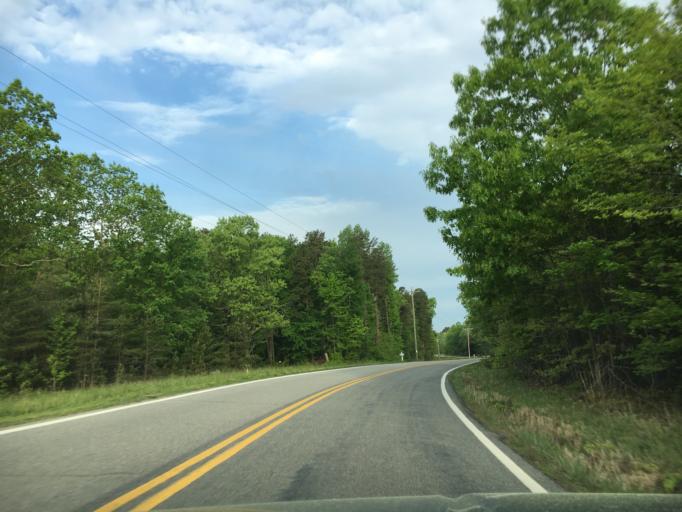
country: US
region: Virginia
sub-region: Halifax County
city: Halifax
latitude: 36.8898
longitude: -78.8036
